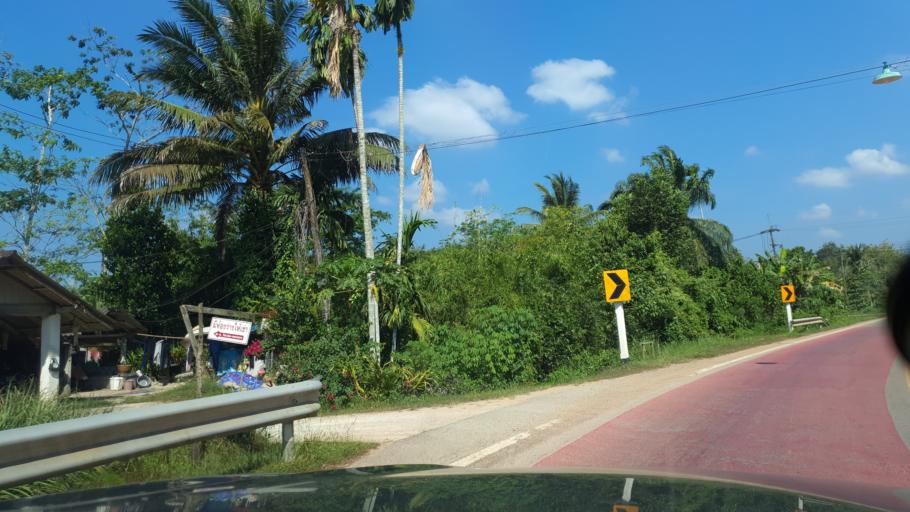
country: TH
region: Phangnga
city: Ban Ao Nang
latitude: 8.0540
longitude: 98.8579
